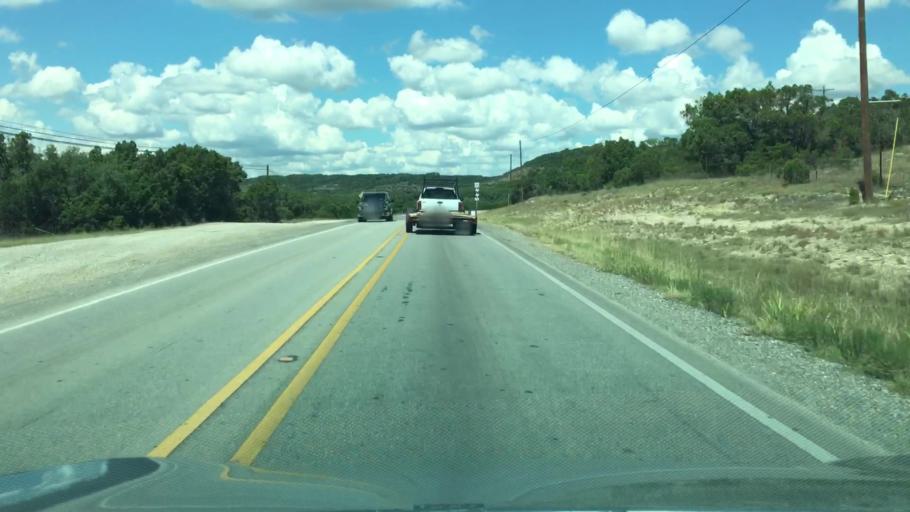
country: US
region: Texas
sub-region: Hays County
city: Wimberley
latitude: 30.0024
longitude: -98.0822
